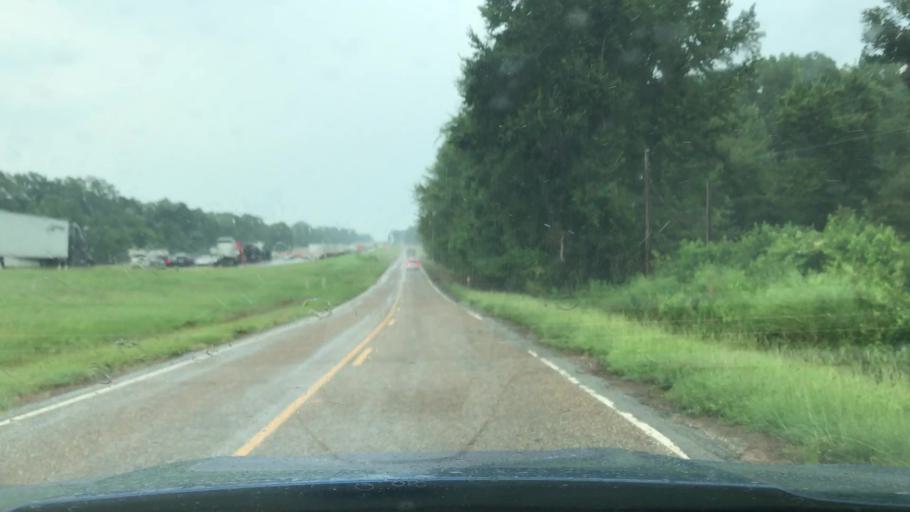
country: US
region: Texas
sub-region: Harrison County
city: Waskom
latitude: 32.4878
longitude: -94.1355
